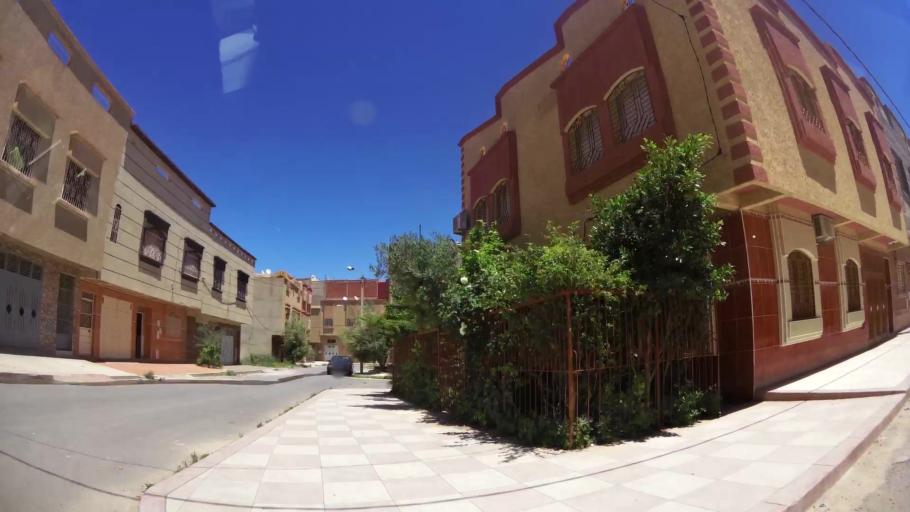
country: MA
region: Oriental
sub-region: Oujda-Angad
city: Oujda
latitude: 34.6801
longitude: -1.8717
